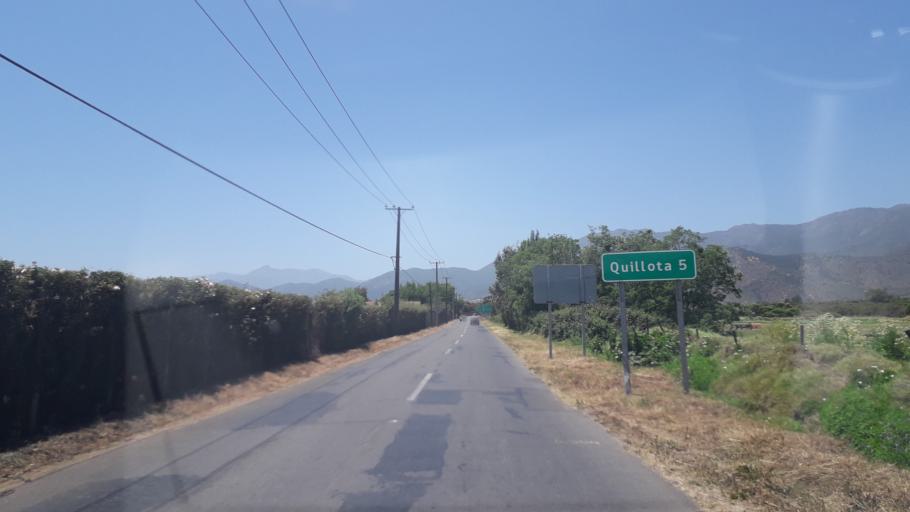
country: CL
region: Valparaiso
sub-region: Provincia de Quillota
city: Quillota
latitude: -32.9109
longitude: -71.2265
